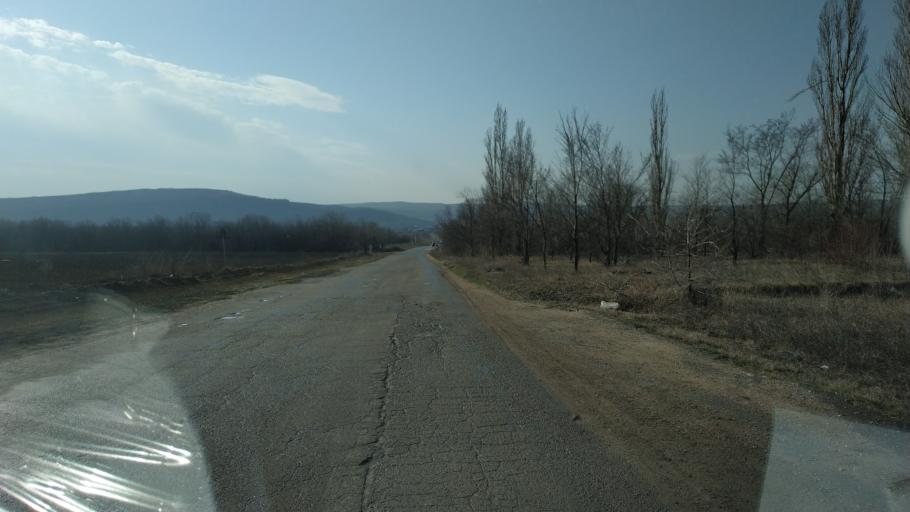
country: MD
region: Chisinau
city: Singera
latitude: 46.6956
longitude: 29.0546
